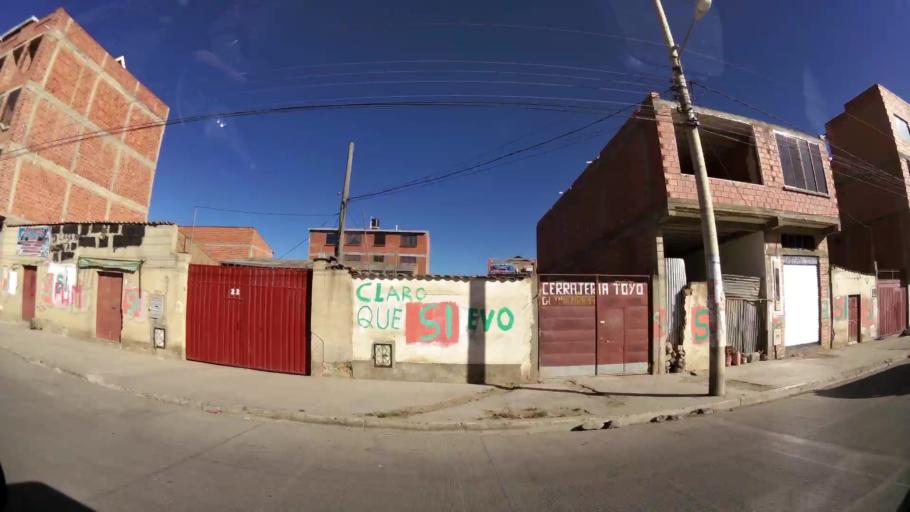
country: BO
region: La Paz
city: La Paz
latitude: -16.5277
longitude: -68.1597
